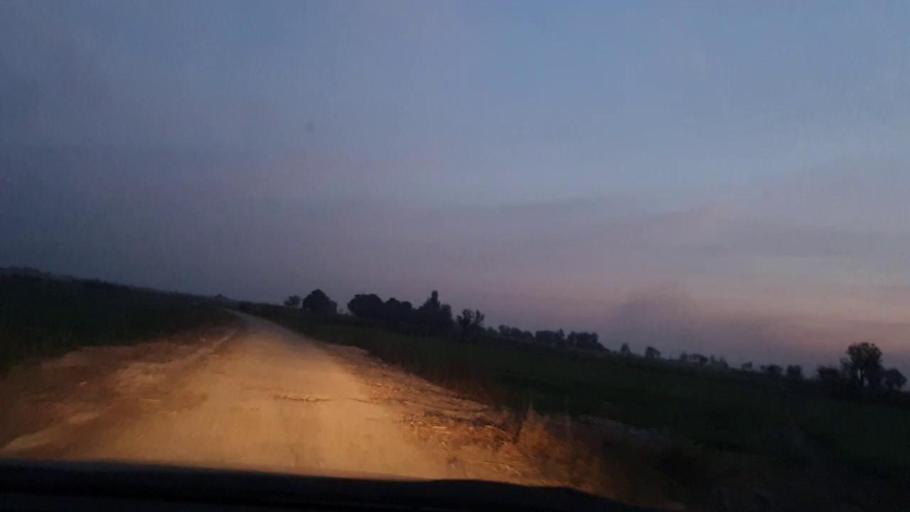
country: PK
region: Sindh
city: Sakrand
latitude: 26.1851
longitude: 68.3052
